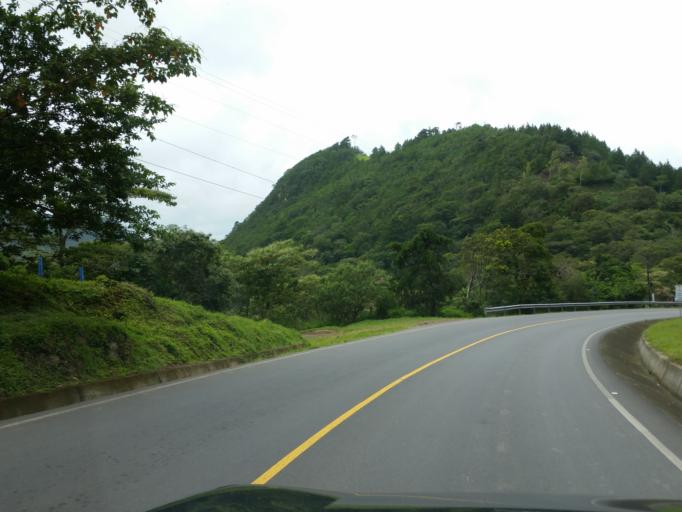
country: NI
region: Matagalpa
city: Matagalpa
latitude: 12.9752
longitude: -85.9207
